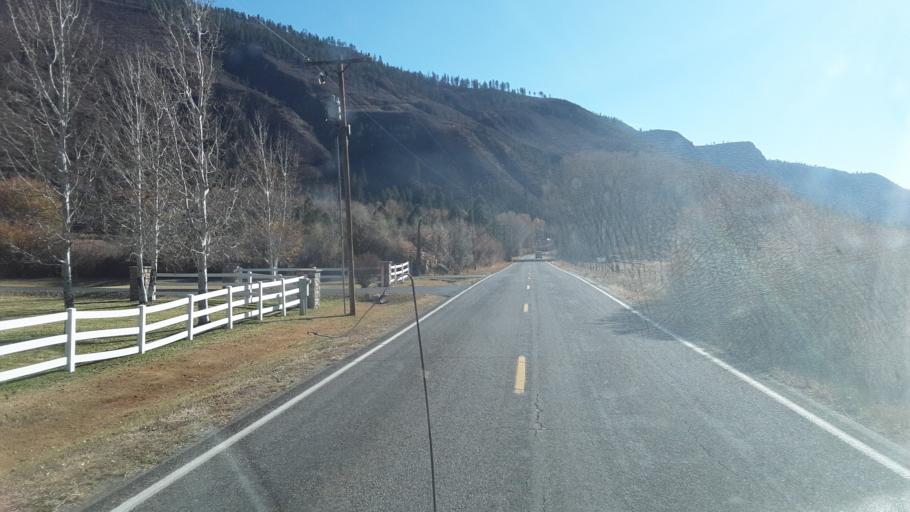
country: US
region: Colorado
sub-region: La Plata County
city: Durango
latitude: 37.4256
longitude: -107.7996
